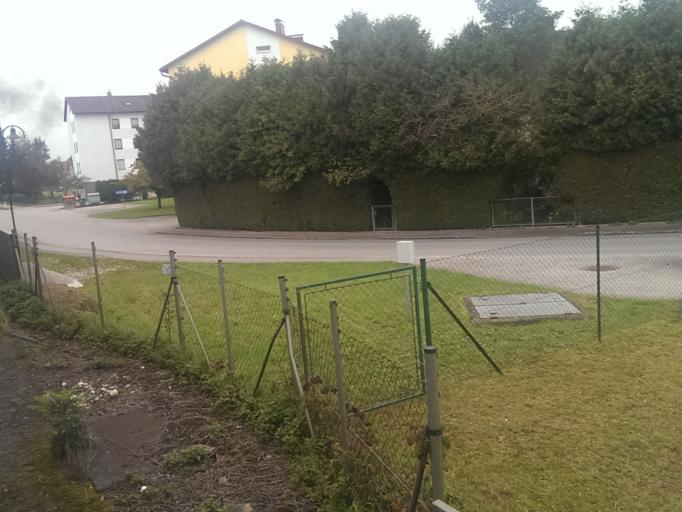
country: AT
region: Upper Austria
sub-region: Politischer Bezirk Vocklabruck
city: Oberndorf bei Schwanenstadt
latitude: 48.0518
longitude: 13.7643
